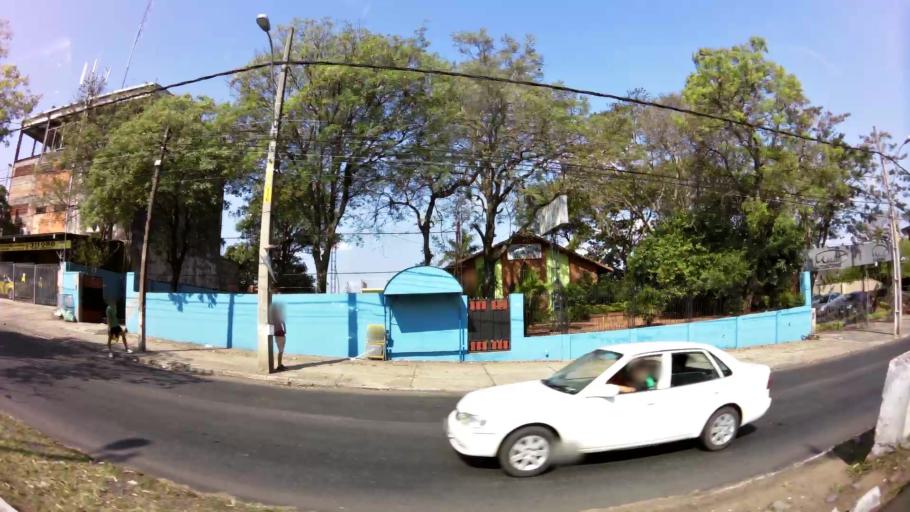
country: PY
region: Asuncion
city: Asuncion
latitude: -25.3091
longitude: -57.6316
